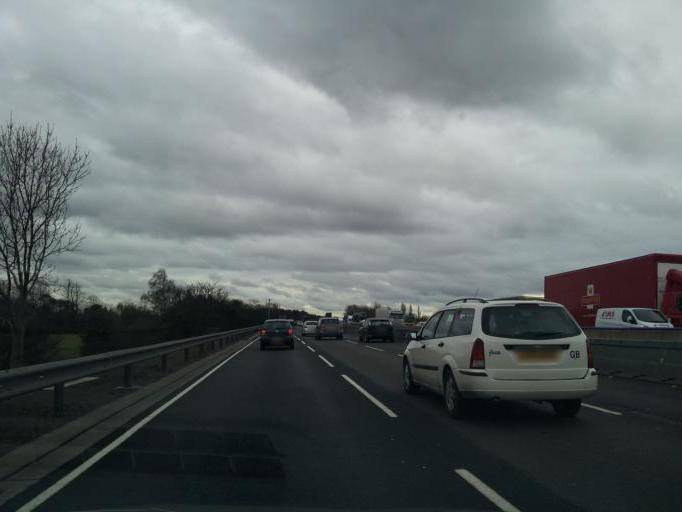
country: GB
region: England
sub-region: Staffordshire
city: Penkridge
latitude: 52.7384
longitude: -2.0983
